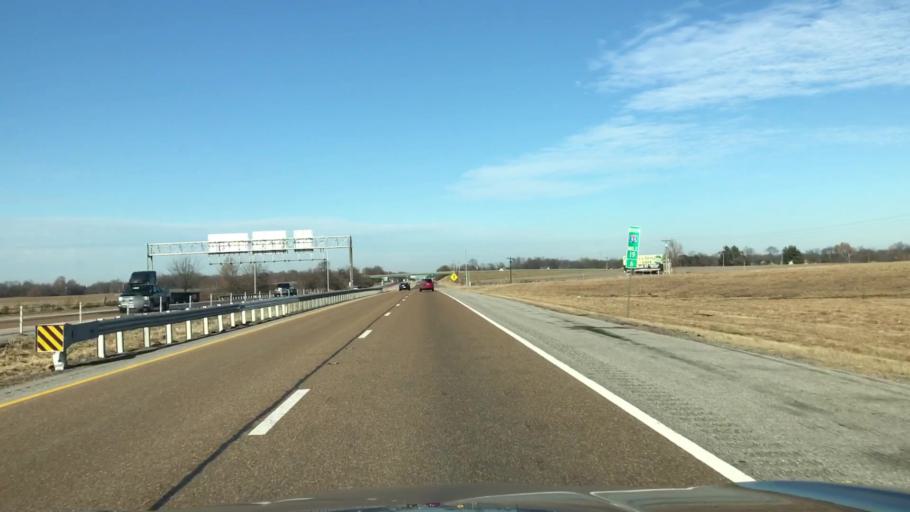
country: US
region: Illinois
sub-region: Madison County
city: Troy
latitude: 38.7540
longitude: -89.9066
